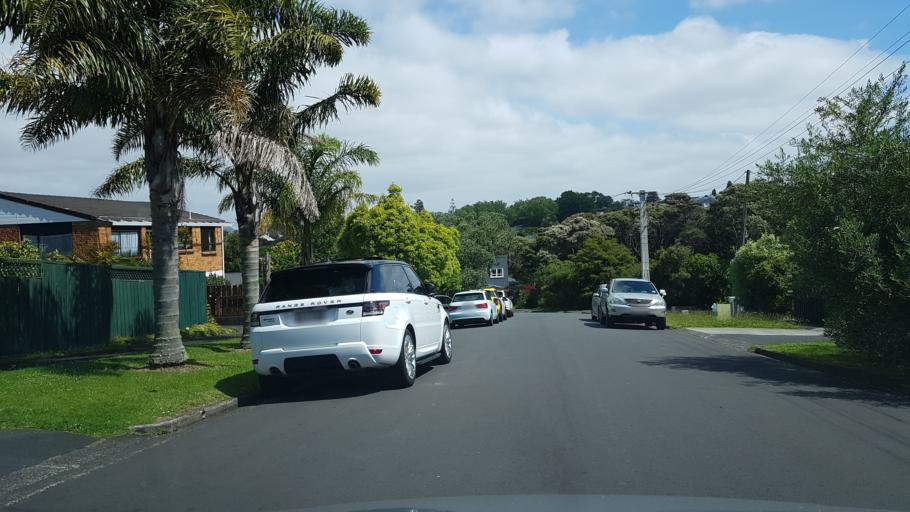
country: NZ
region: Auckland
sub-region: Auckland
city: North Shore
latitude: -36.8115
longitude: 174.7330
